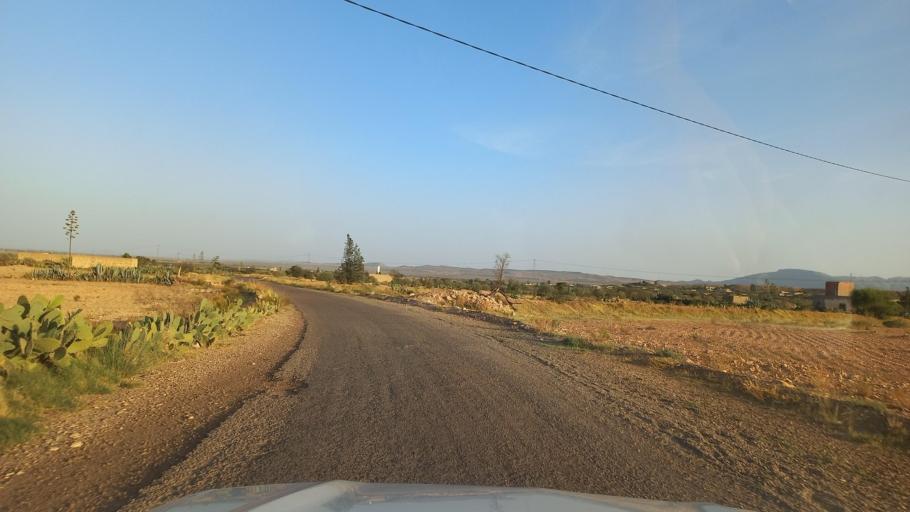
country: TN
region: Al Qasrayn
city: Kasserine
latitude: 35.2707
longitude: 8.9287
